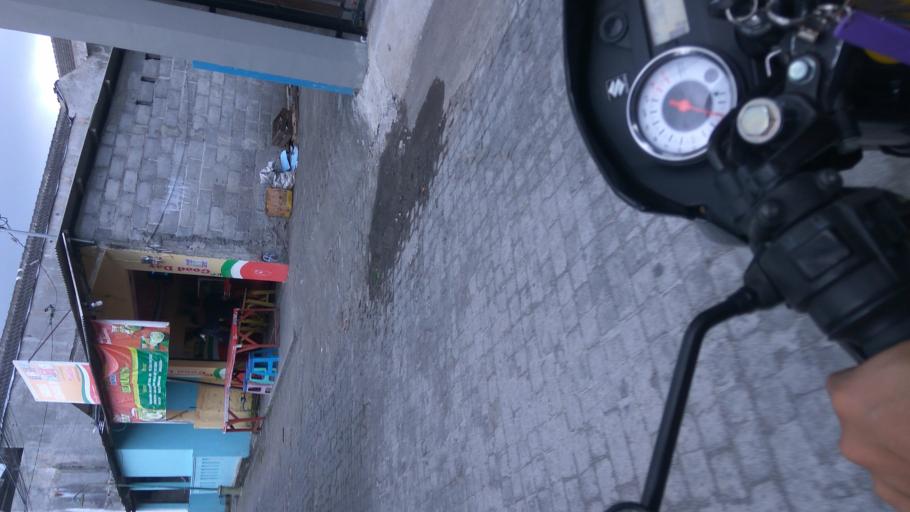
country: ID
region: Daerah Istimewa Yogyakarta
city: Depok
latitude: -7.7567
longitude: 110.4133
